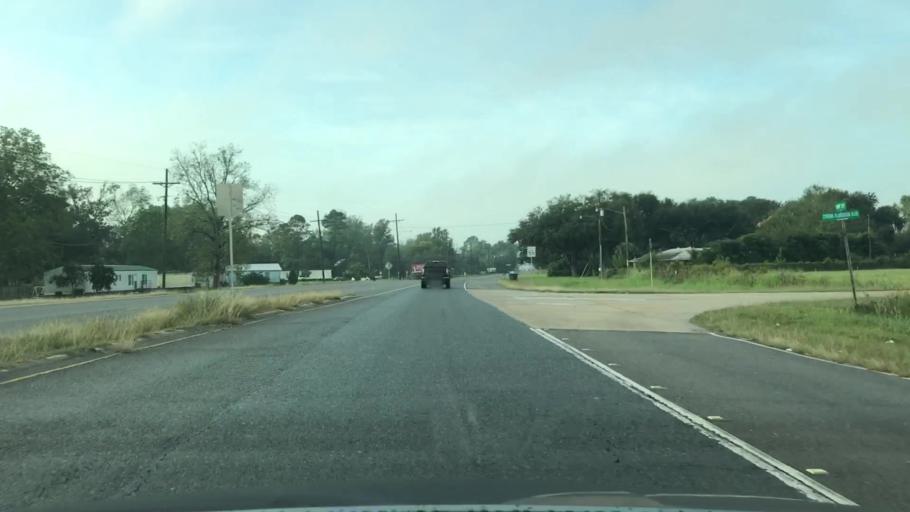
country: US
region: Louisiana
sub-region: Terrebonne Parish
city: Gray
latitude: 29.6767
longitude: -90.8135
